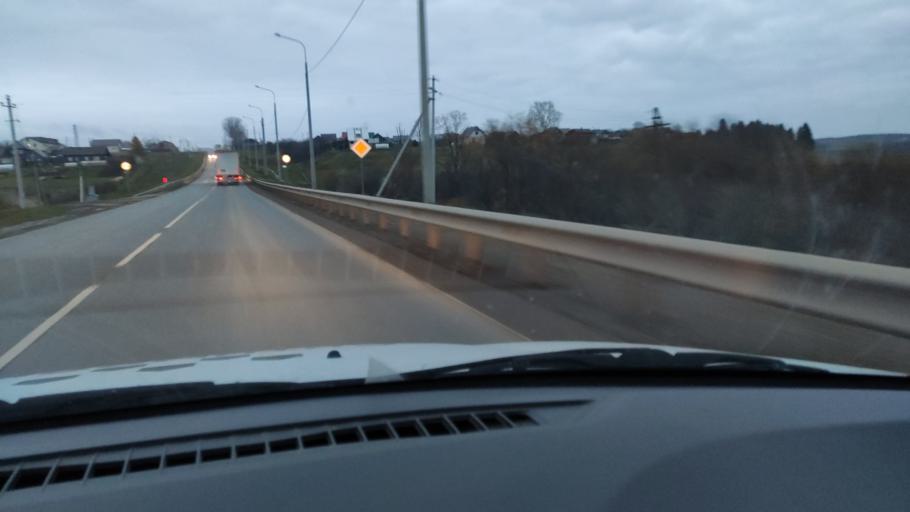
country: RU
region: Kirov
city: Kostino
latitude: 58.8545
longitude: 53.2344
